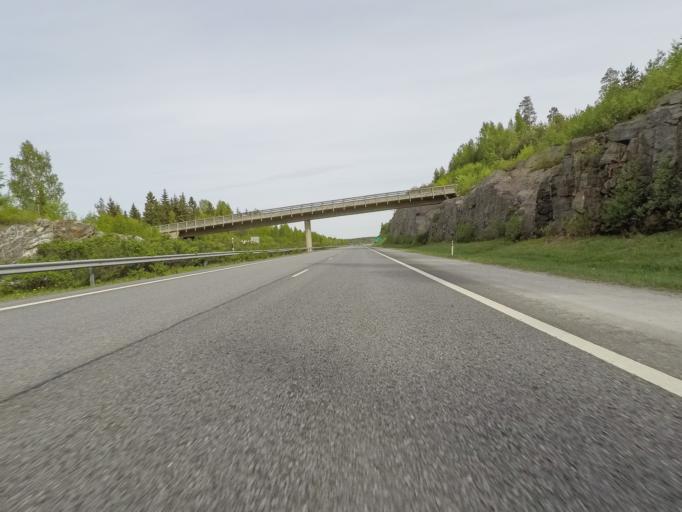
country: FI
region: Pirkanmaa
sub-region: Etelae-Pirkanmaa
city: Akaa
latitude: 61.1766
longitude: 23.9123
